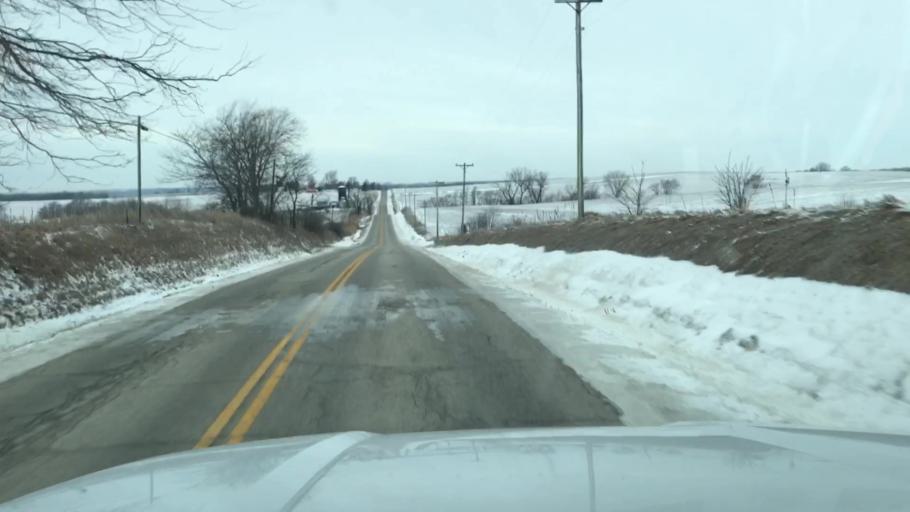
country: US
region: Missouri
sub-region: Andrew County
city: Savannah
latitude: 40.0249
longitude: -94.9446
